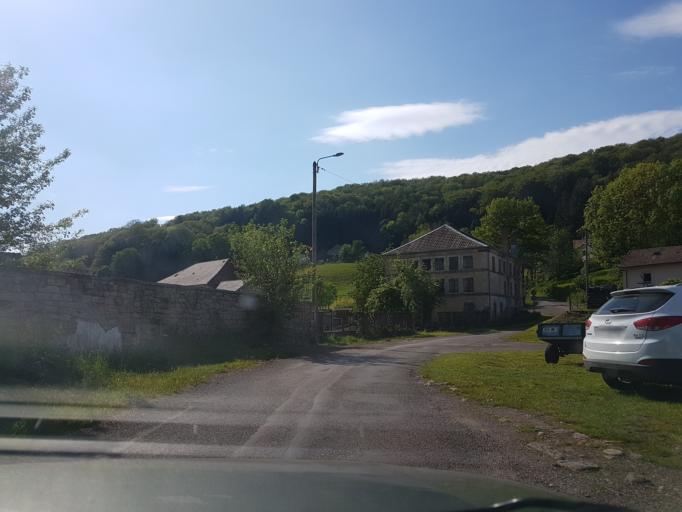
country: FR
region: Franche-Comte
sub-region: Departement de la Haute-Saone
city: Froideconche
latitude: 47.8597
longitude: 6.4852
